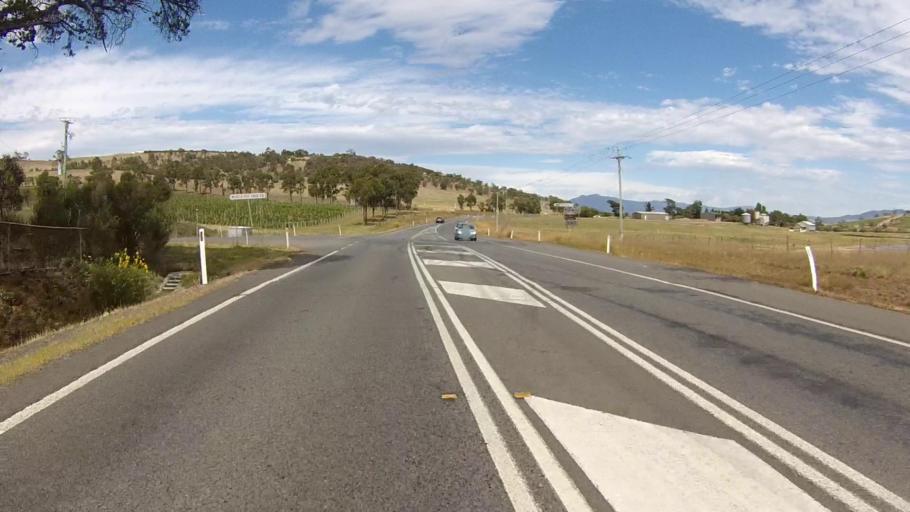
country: AU
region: Tasmania
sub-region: Brighton
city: Old Beach
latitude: -42.6912
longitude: 147.3446
